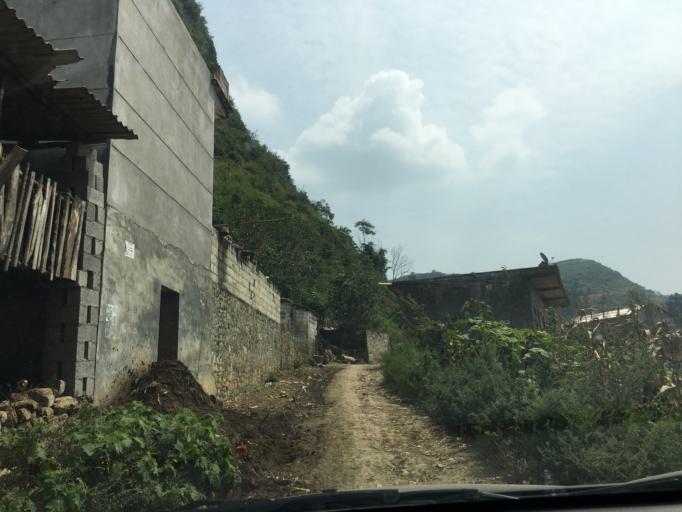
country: CN
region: Guizhou Sheng
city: Anshun
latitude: 25.5964
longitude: 105.6701
